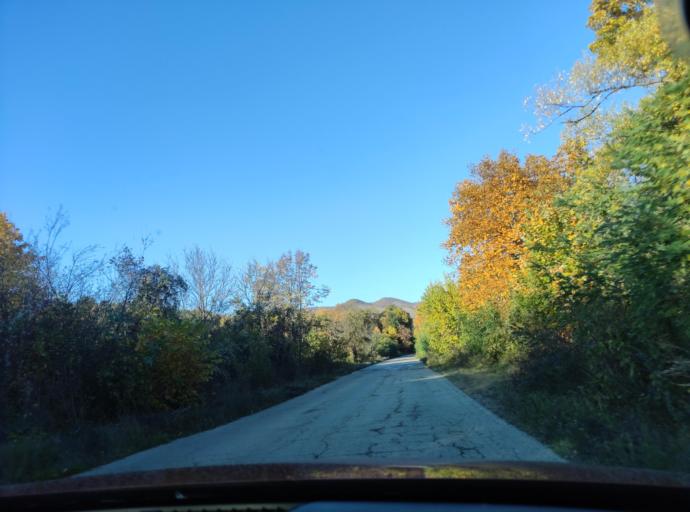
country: BG
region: Montana
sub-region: Obshtina Chiprovtsi
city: Chiprovtsi
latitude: 43.4226
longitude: 22.9555
